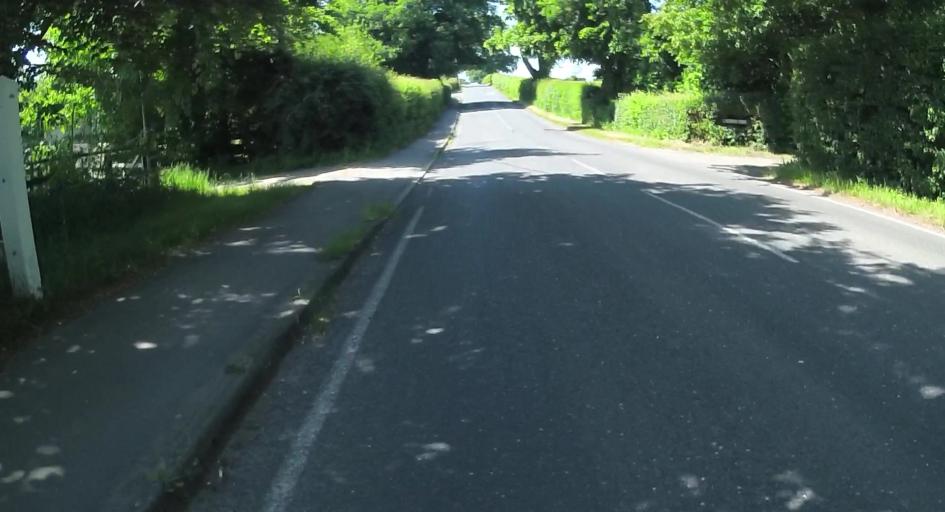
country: GB
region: England
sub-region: Hampshire
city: Kingsclere
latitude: 51.3551
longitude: -1.2091
